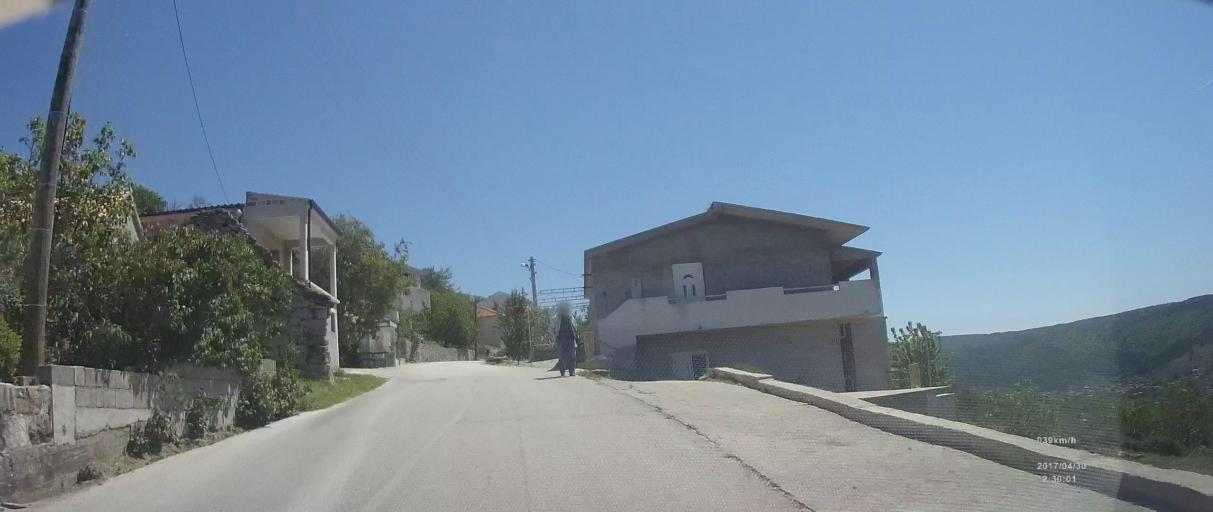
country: HR
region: Splitsko-Dalmatinska
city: Srinjine
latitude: 43.5013
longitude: 16.6030
